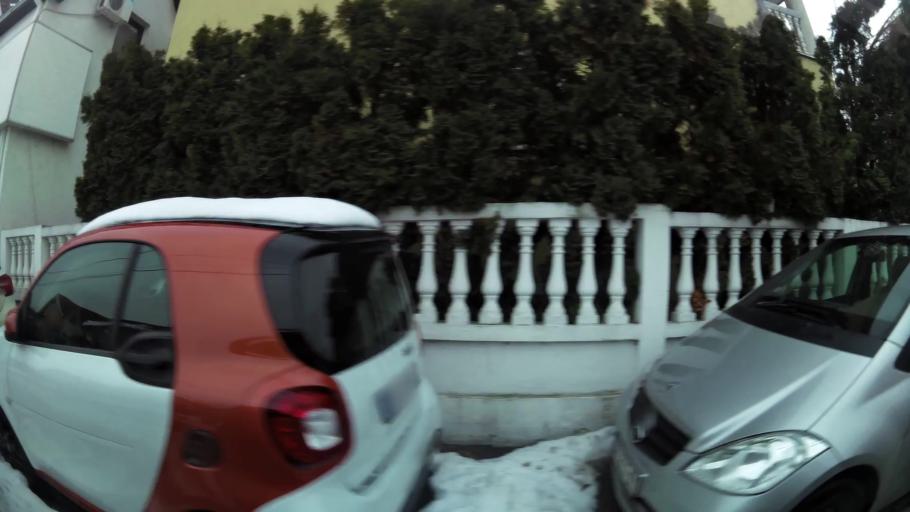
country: RS
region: Central Serbia
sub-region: Belgrade
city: Vozdovac
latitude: 44.7691
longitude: 20.5034
